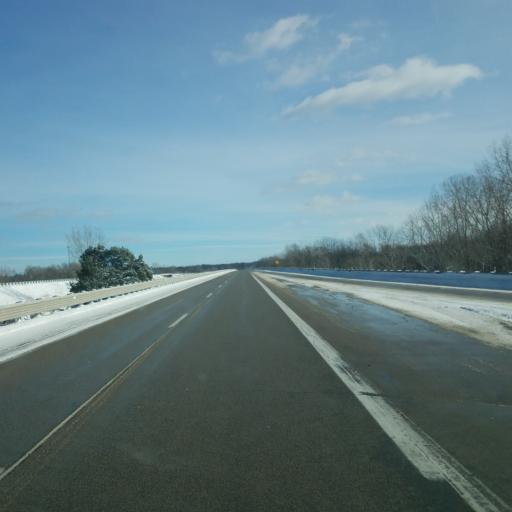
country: US
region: Michigan
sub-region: Clare County
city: Clare
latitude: 43.8658
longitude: -84.9055
